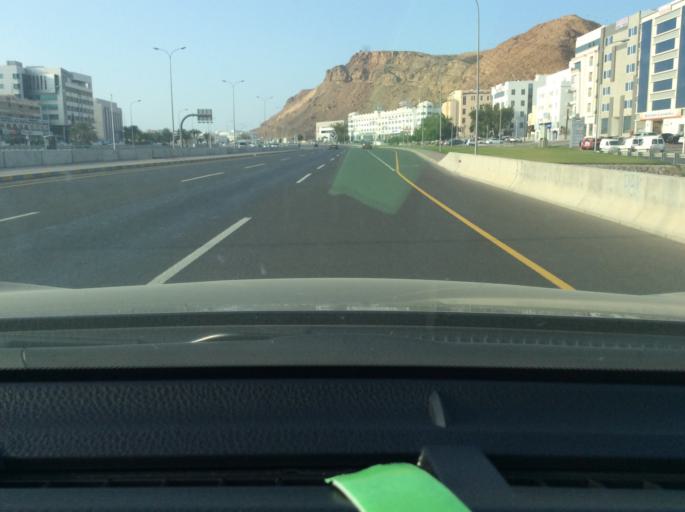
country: OM
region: Muhafazat Masqat
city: Muscat
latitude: 23.5963
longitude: 58.5211
